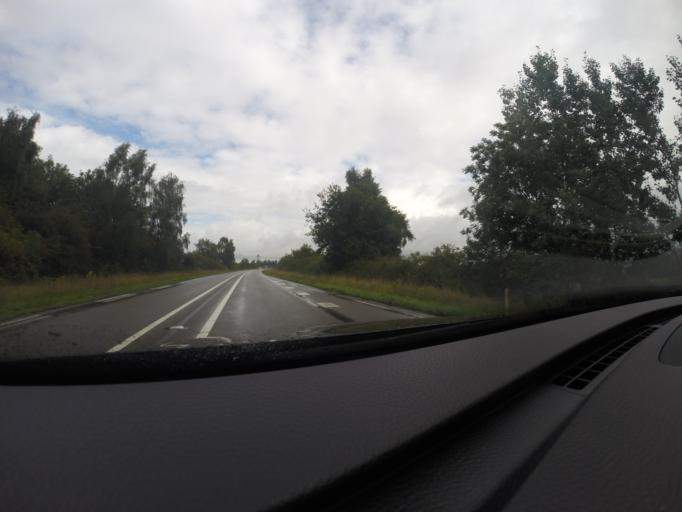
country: NL
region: Gelderland
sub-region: Gemeente Lochem
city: Laren
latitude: 52.2523
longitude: 6.3987
